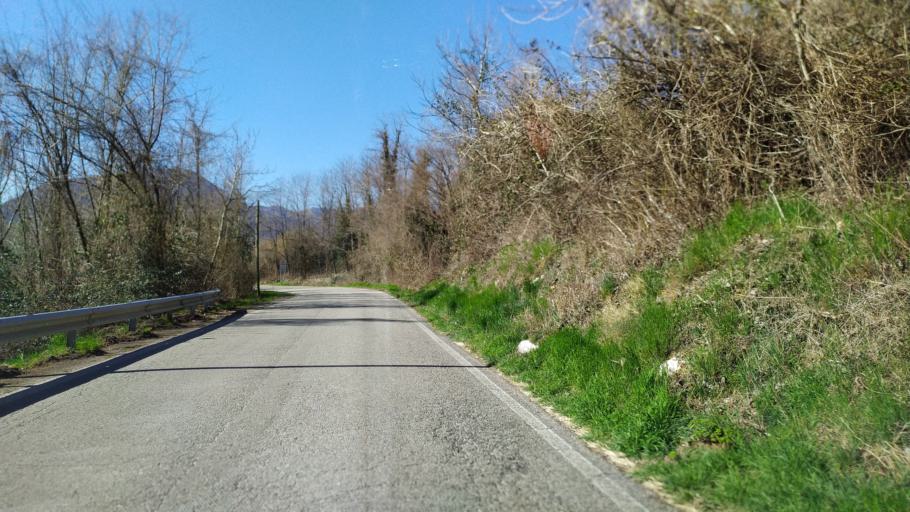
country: IT
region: Veneto
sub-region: Provincia di Vicenza
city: Calvene
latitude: 45.7659
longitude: 11.4857
